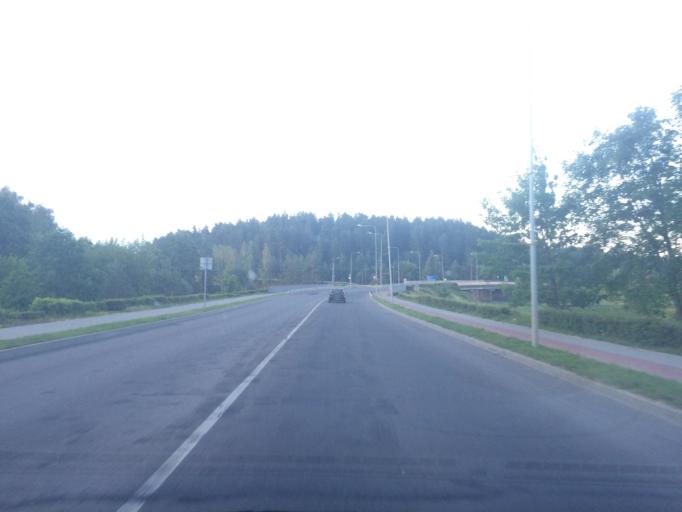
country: LT
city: Zarasai
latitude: 55.7260
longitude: 26.2461
